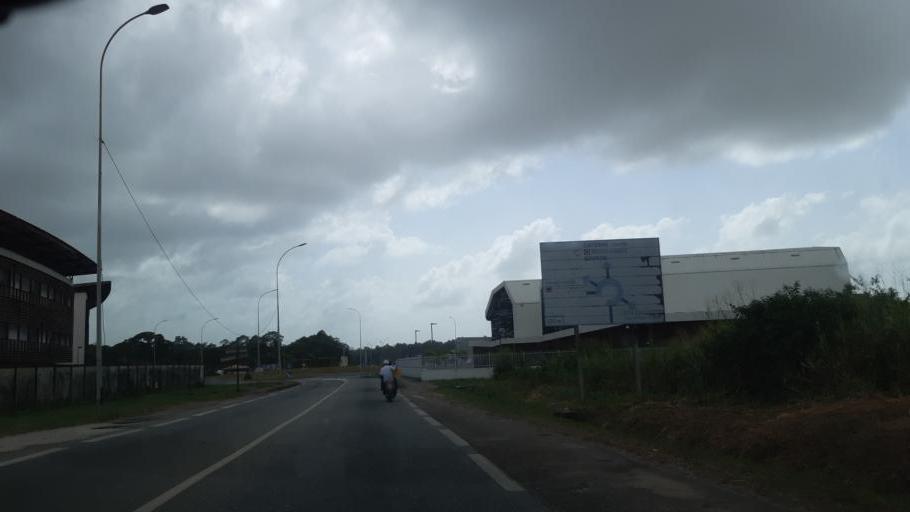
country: GF
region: Guyane
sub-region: Guyane
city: Cayenne
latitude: 4.9256
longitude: -52.3223
